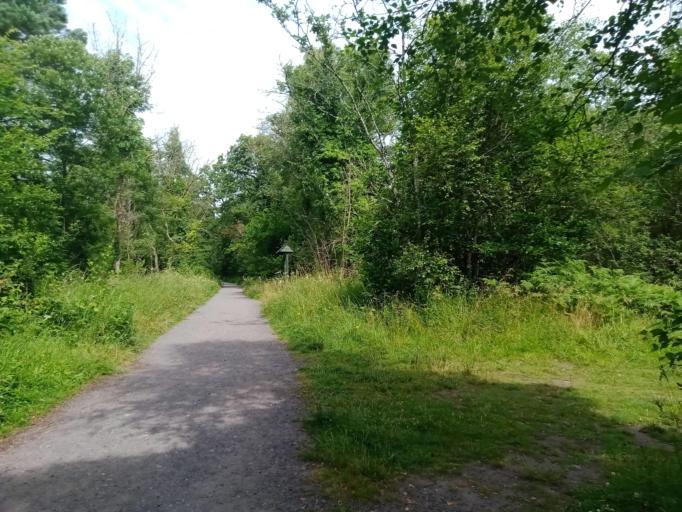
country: IE
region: Leinster
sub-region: Laois
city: Abbeyleix
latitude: 52.9040
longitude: -7.3518
